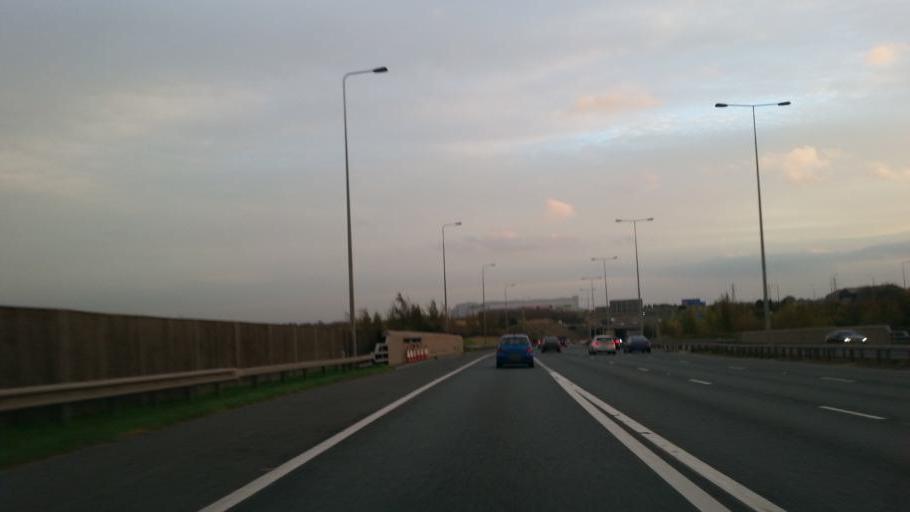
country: GB
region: England
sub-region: City and Borough of Wakefield
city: Ferrybridge
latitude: 53.7039
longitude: -1.2772
